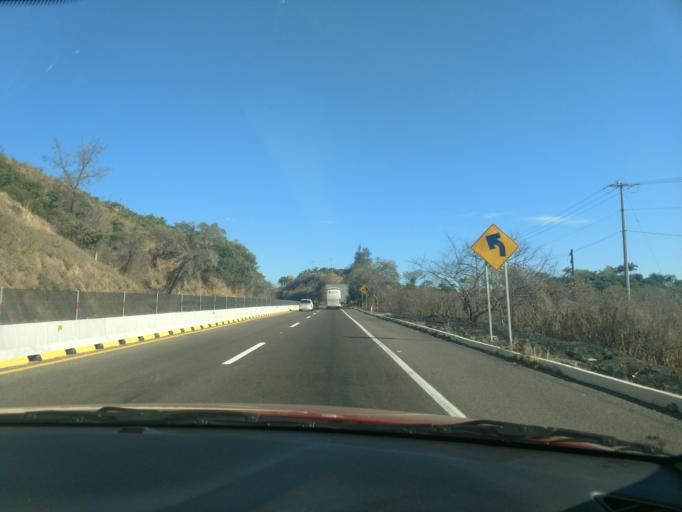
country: MX
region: Nayarit
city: Tepic
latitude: 21.5554
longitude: -104.9602
